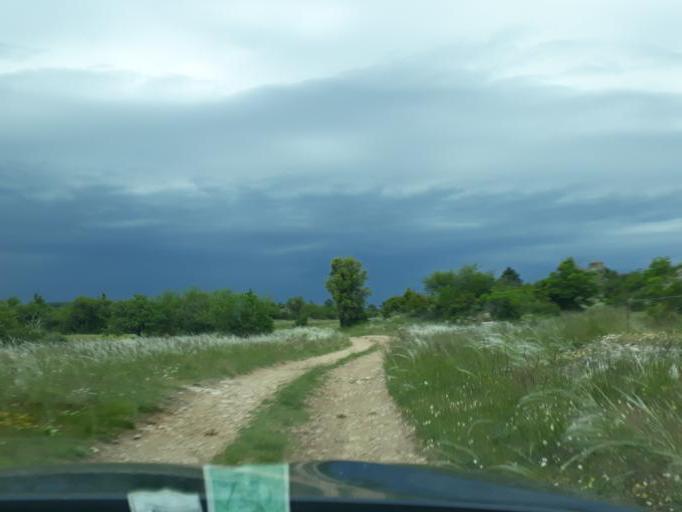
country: FR
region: Languedoc-Roussillon
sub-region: Departement de l'Herault
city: Lodeve
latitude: 43.8185
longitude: 3.2771
